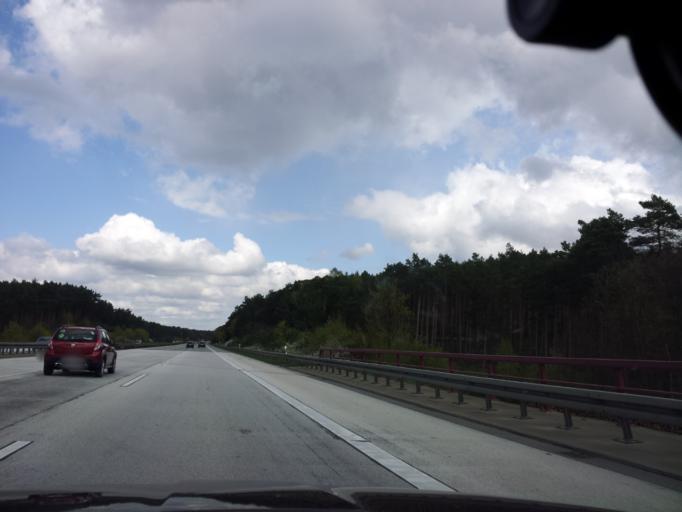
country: DE
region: Brandenburg
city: Erkner
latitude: 52.3542
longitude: 13.7588
